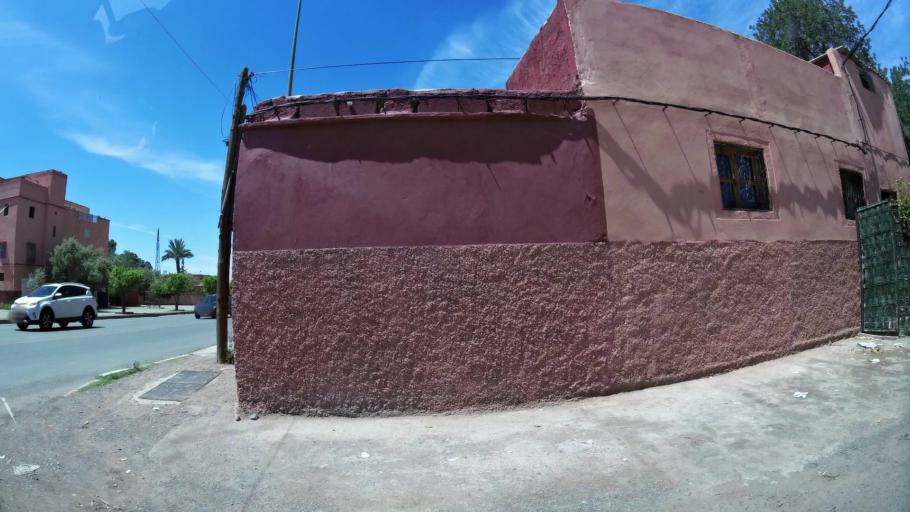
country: MA
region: Marrakech-Tensift-Al Haouz
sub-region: Marrakech
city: Marrakesh
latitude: 31.6357
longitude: -8.0470
